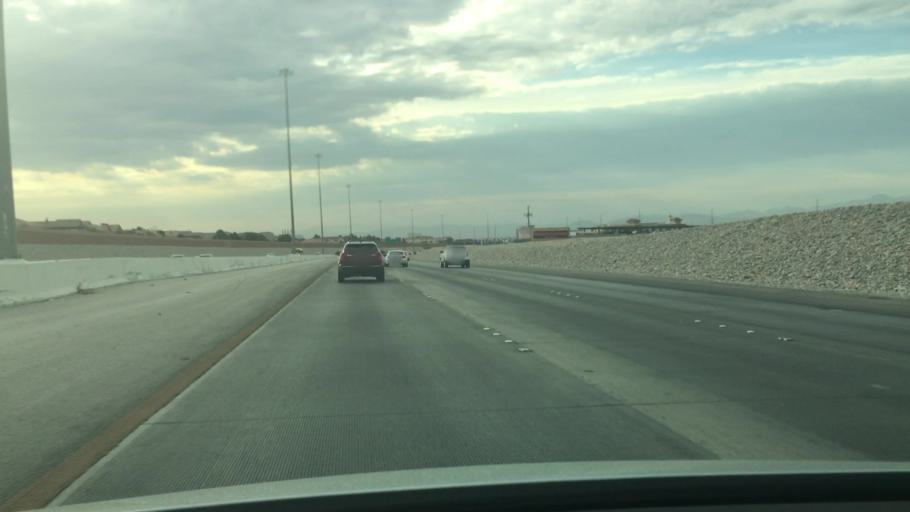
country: US
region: Nevada
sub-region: Clark County
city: Summerlin South
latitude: 36.1187
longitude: -115.3144
